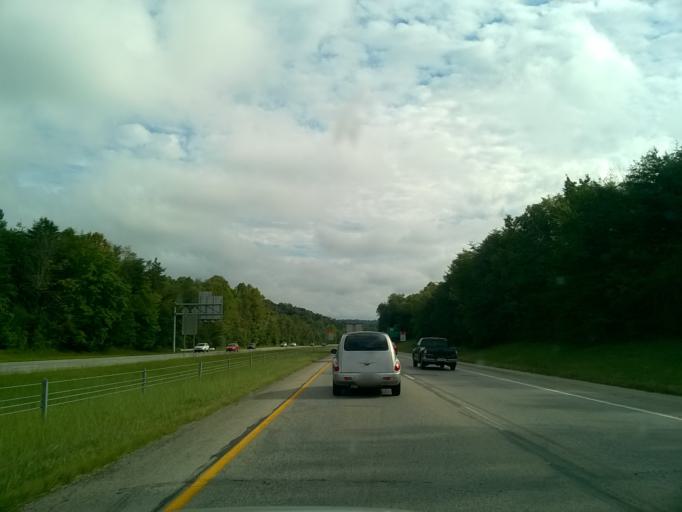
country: US
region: Indiana
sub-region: Floyd County
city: Galena
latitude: 38.3003
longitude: -85.8966
